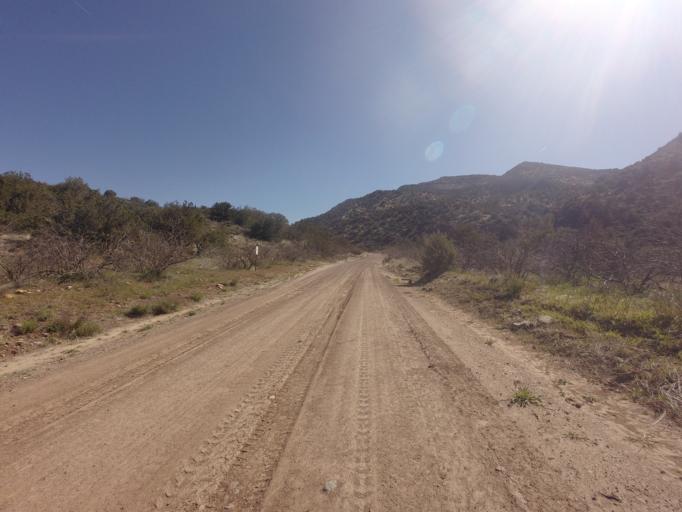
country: US
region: Arizona
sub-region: Gila County
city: Pine
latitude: 34.3937
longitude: -111.6336
